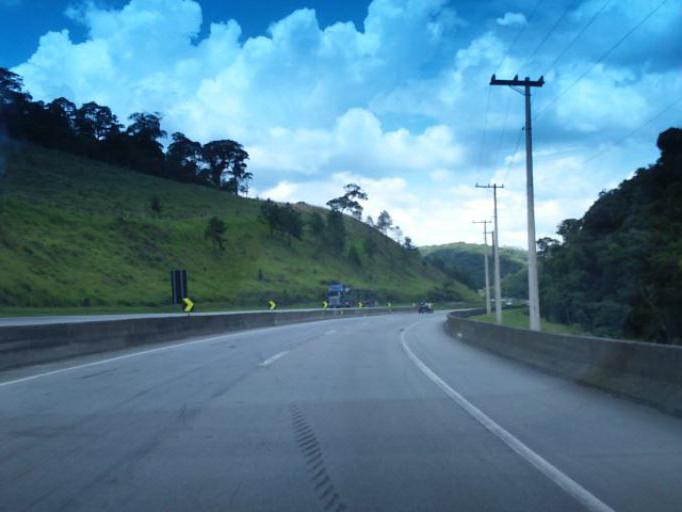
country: BR
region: Sao Paulo
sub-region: Juquitiba
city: Juquitiba
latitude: -24.0023
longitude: -47.1526
